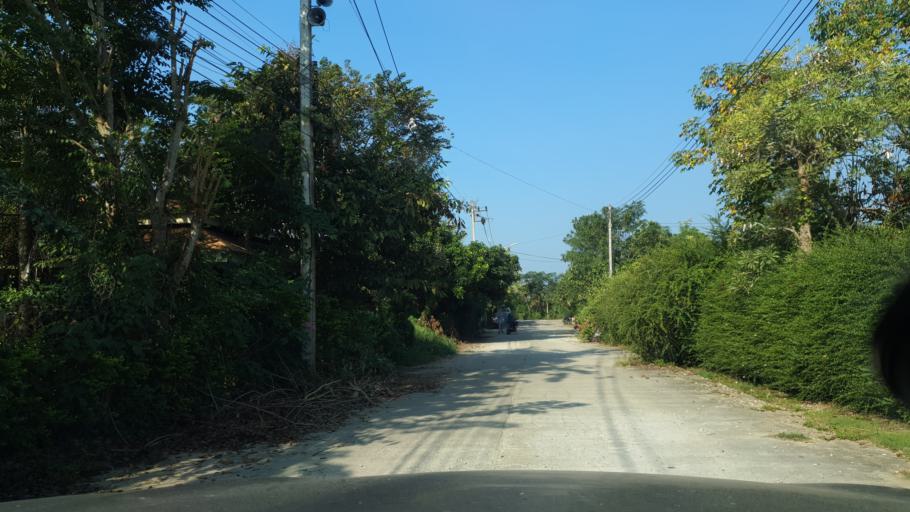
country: TH
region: Chiang Mai
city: Saraphi
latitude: 18.7139
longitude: 98.9936
